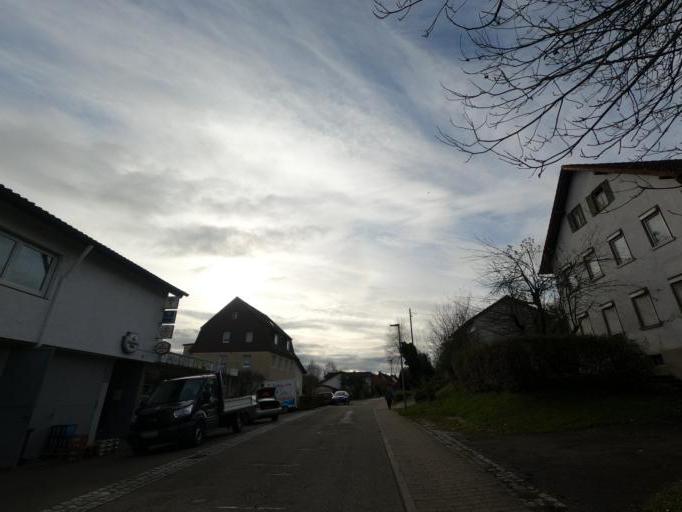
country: DE
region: Baden-Wuerttemberg
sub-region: Regierungsbezirk Stuttgart
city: Albershausen
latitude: 48.6894
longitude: 9.5615
